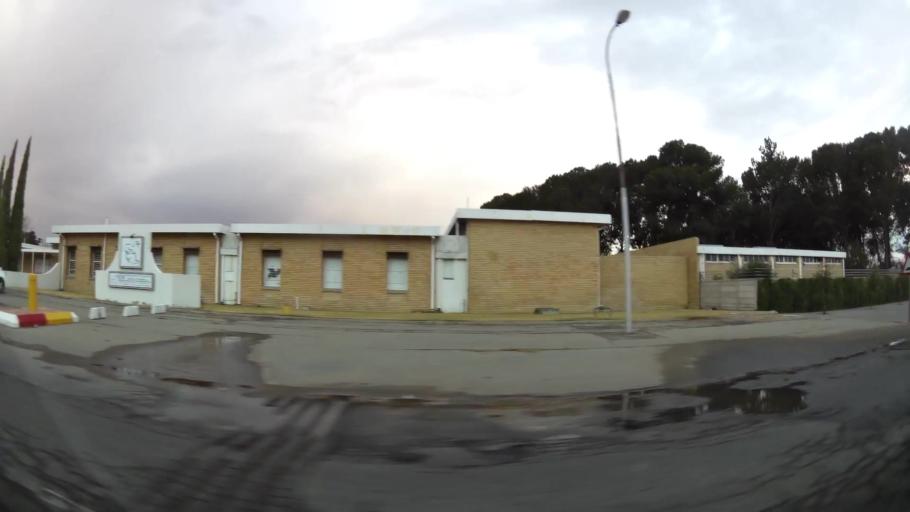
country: ZA
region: Orange Free State
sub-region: Lejweleputswa District Municipality
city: Welkom
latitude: -27.9551
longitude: 26.7582
